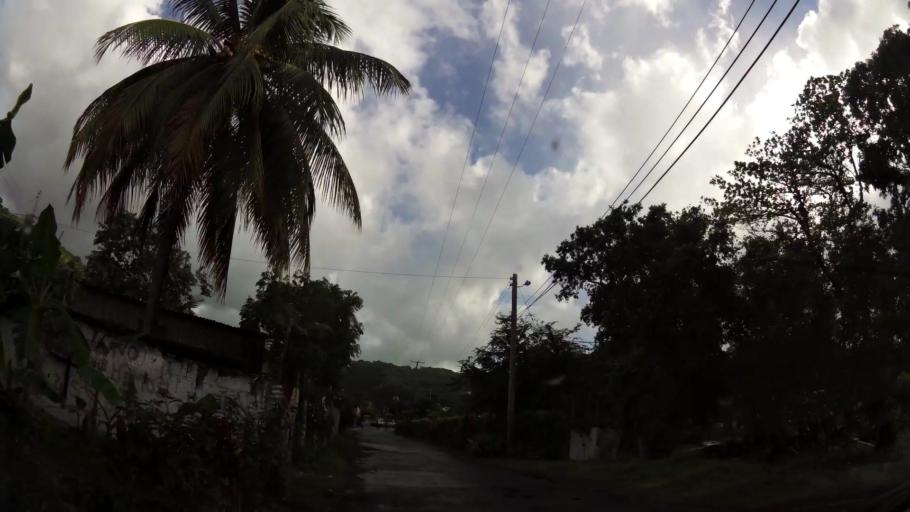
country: DM
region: Saint George
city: Roseau
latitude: 15.3313
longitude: -61.3896
